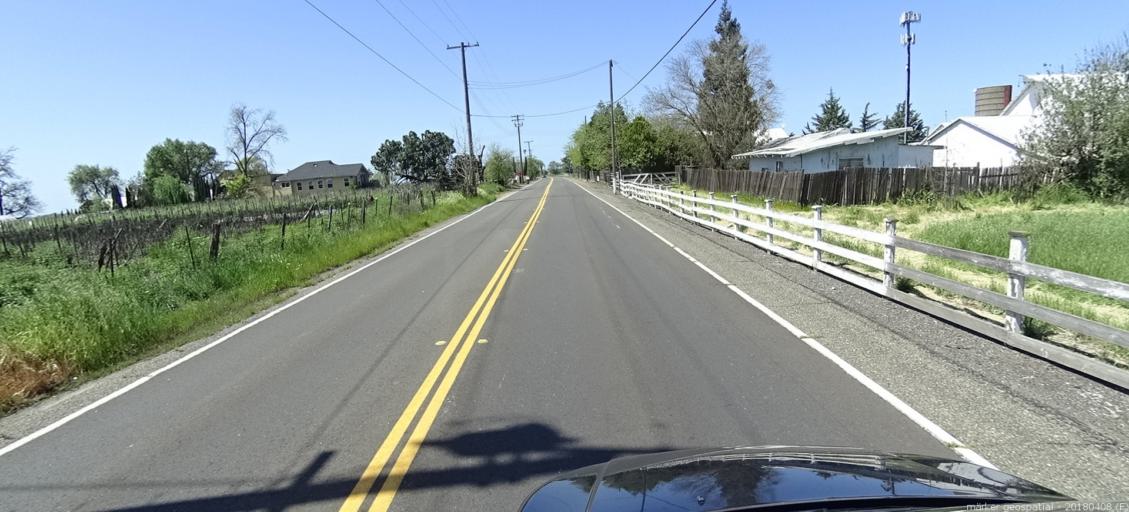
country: US
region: California
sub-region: Sacramento County
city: Laguna
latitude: 38.3761
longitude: -121.4656
